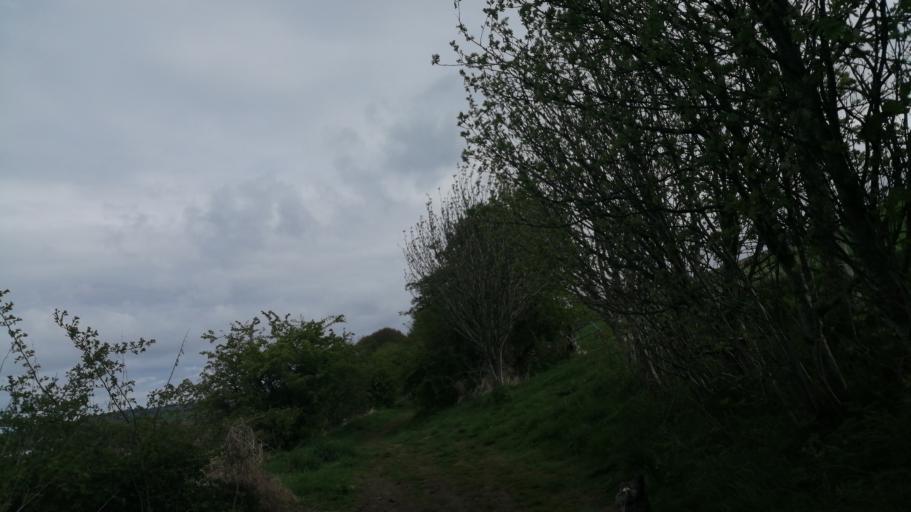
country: GB
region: Scotland
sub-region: Moray
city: Keith
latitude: 57.5334
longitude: -2.9612
